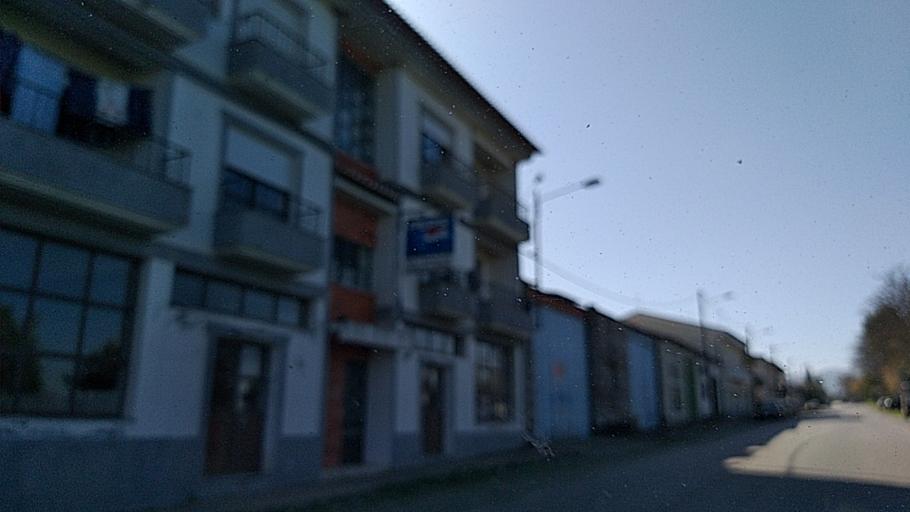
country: PT
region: Guarda
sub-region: Celorico da Beira
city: Celorico da Beira
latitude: 40.6637
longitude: -7.3816
